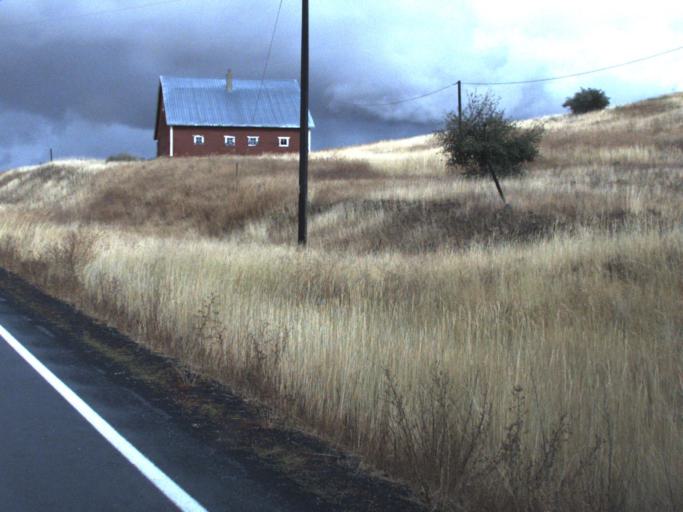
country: US
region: Washington
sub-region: Spokane County
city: Medical Lake
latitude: 47.6883
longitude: -117.8819
